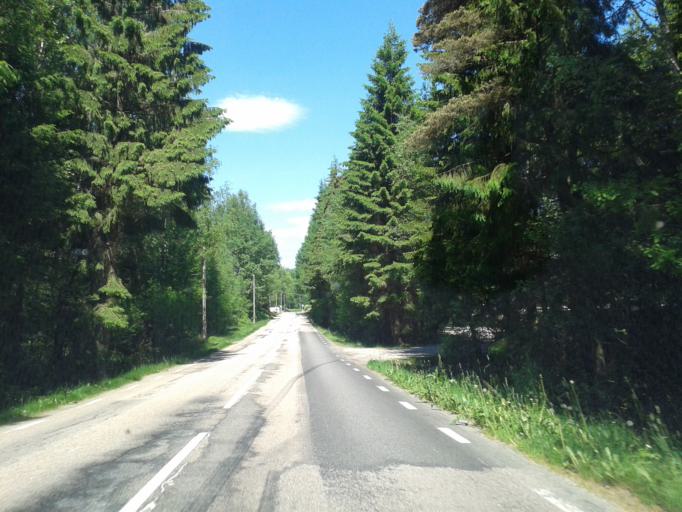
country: SE
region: Vaestra Goetaland
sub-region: Orust
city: Henan
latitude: 58.2786
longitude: 11.7175
